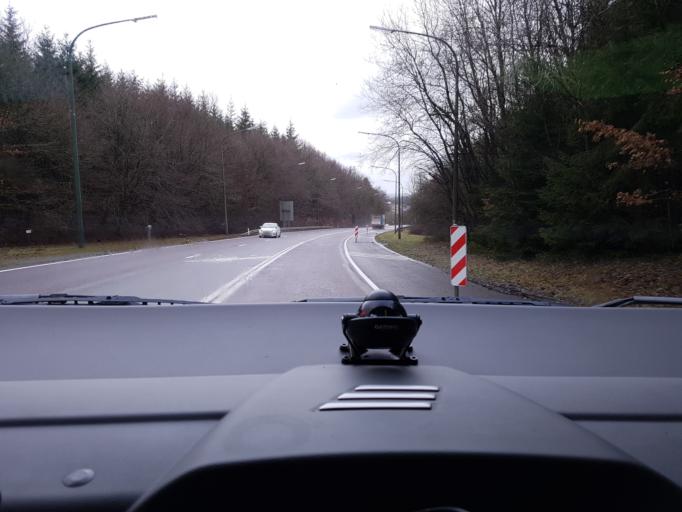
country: BE
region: Wallonia
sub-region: Province du Luxembourg
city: Martelange
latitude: 49.8124
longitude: 5.7386
